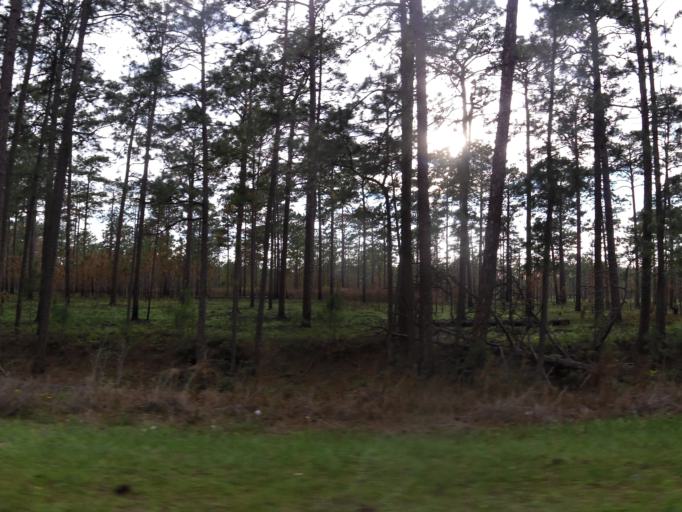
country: US
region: South Carolina
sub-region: Jasper County
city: Hardeeville
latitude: 32.3471
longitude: -81.0926
